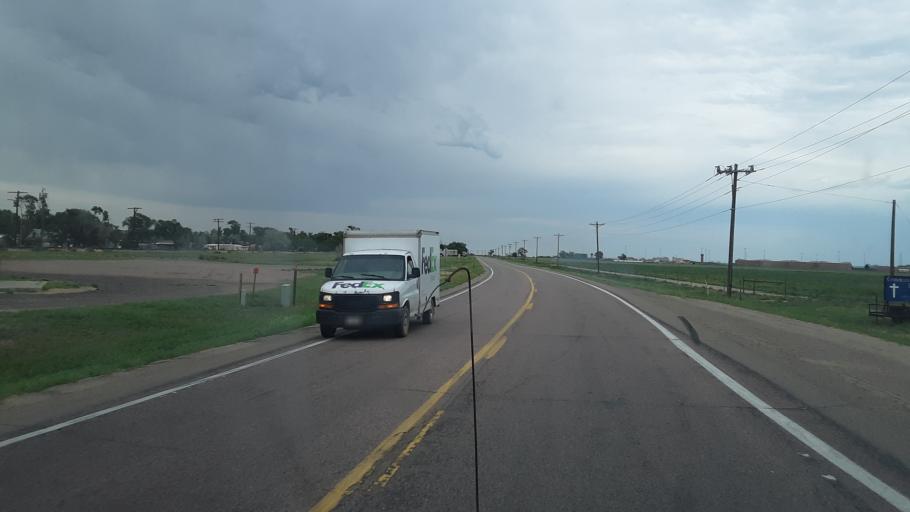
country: US
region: Colorado
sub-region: Crowley County
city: Ordway
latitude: 38.1915
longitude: -103.8574
